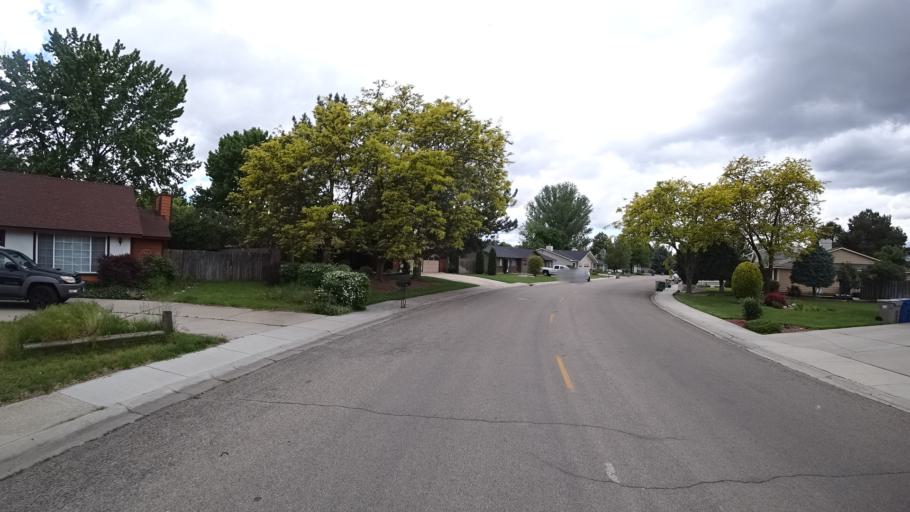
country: US
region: Idaho
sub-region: Ada County
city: Garden City
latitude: 43.6598
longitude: -116.2580
